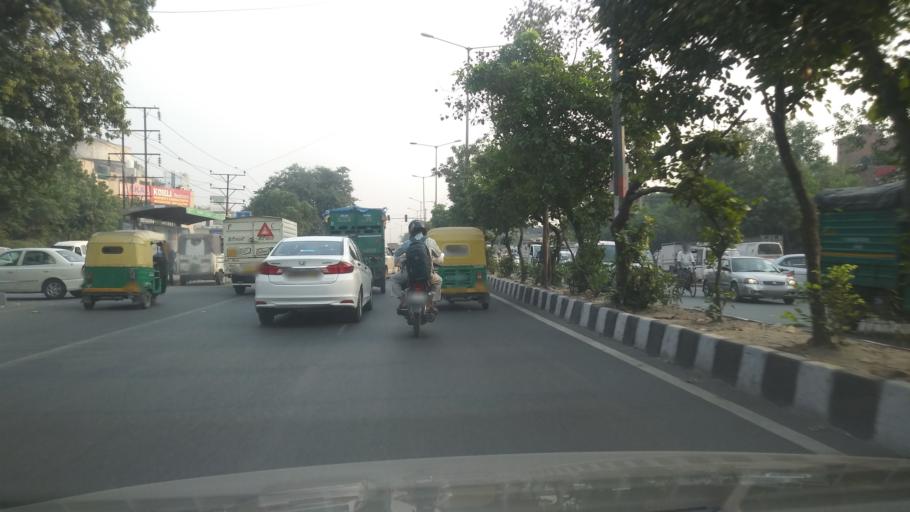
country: IN
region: Uttar Pradesh
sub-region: Gautam Buddha Nagar
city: Noida
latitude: 28.5343
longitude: 77.2685
